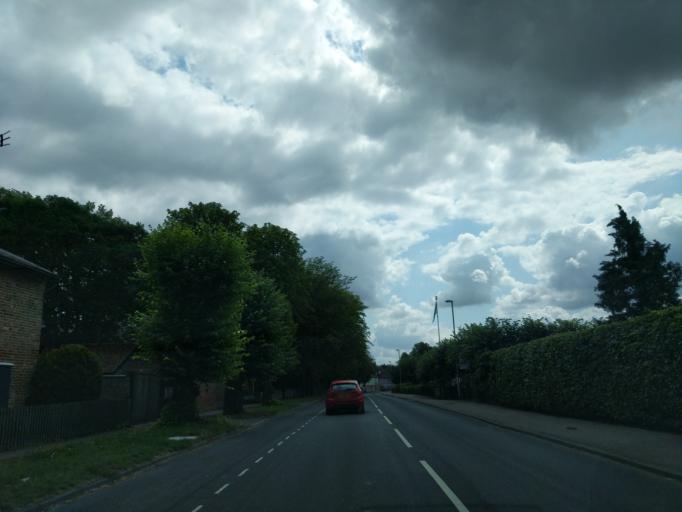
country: GB
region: England
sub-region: Cambridgeshire
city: Isleham
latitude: 52.3013
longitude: 0.4371
